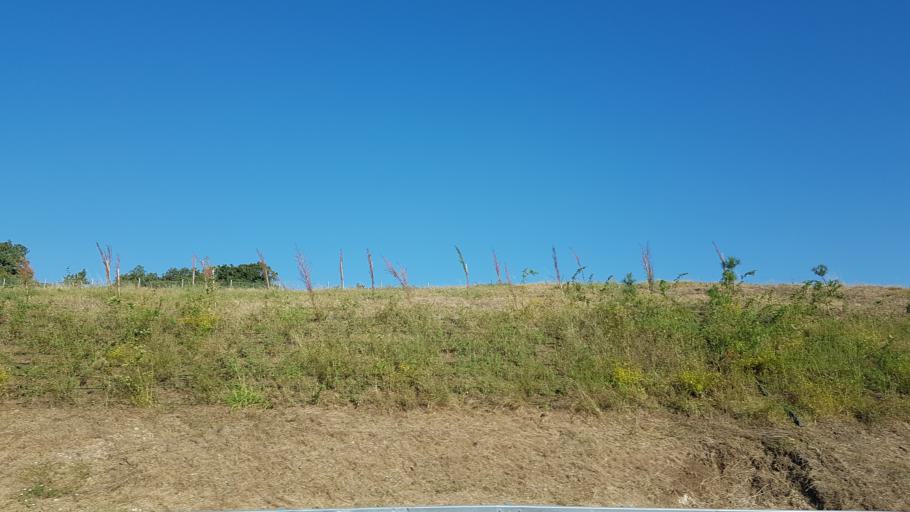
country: TR
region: Balikesir
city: Ertugrul
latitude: 39.6411
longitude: 27.7182
